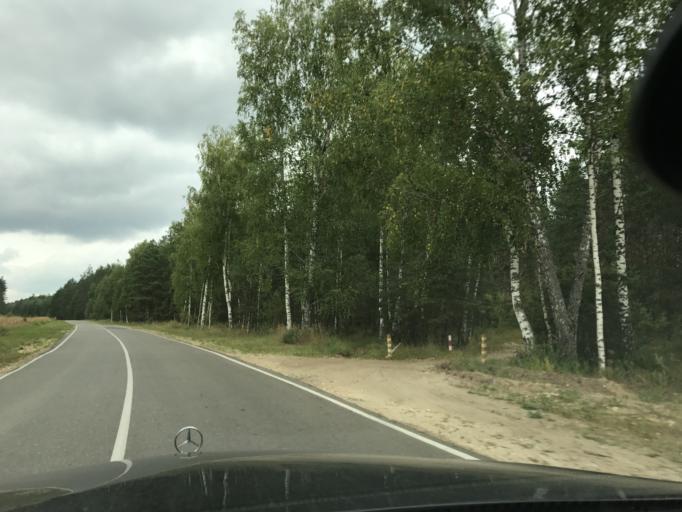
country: RU
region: Nizjnij Novgorod
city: Taremskoye
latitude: 56.0110
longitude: 42.9780
